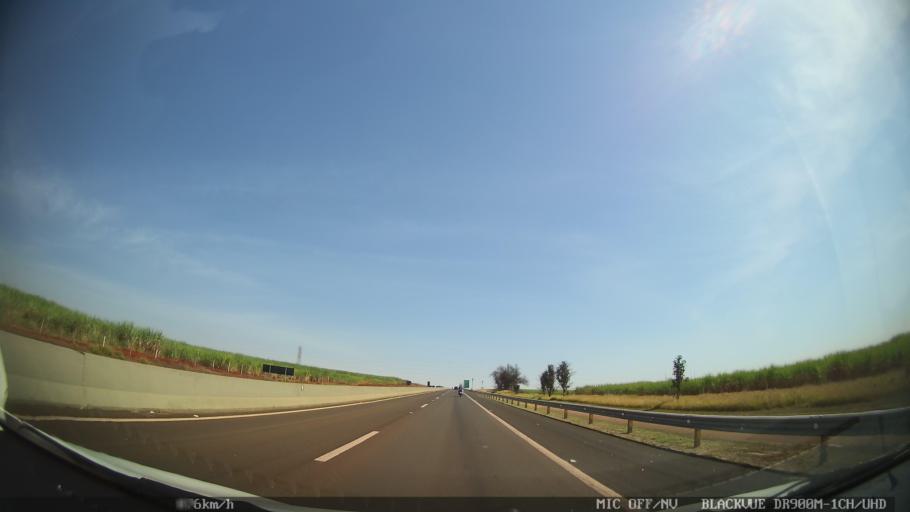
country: BR
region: Sao Paulo
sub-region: Ribeirao Preto
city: Ribeirao Preto
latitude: -21.1660
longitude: -47.8848
